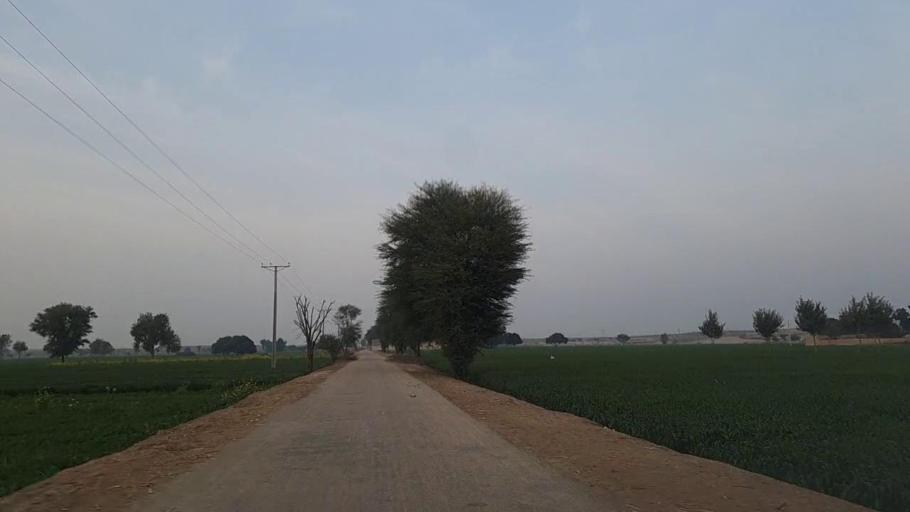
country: PK
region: Sindh
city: Jam Sahib
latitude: 26.4696
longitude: 68.5481
